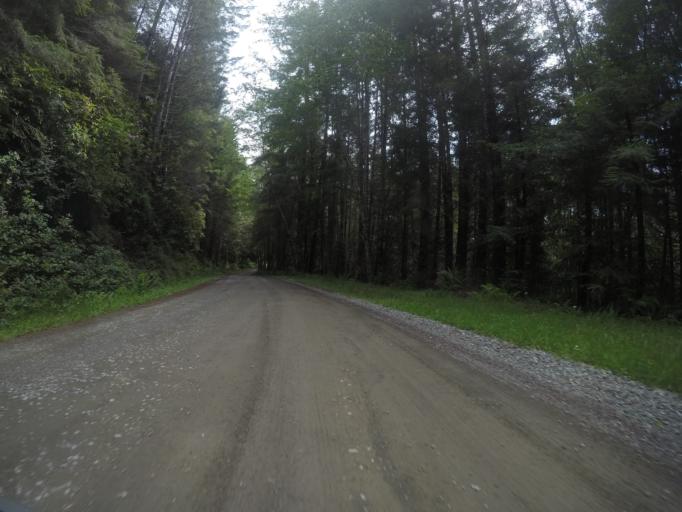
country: US
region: California
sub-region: Humboldt County
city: Westhaven-Moonstone
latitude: 41.2269
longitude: -124.0020
